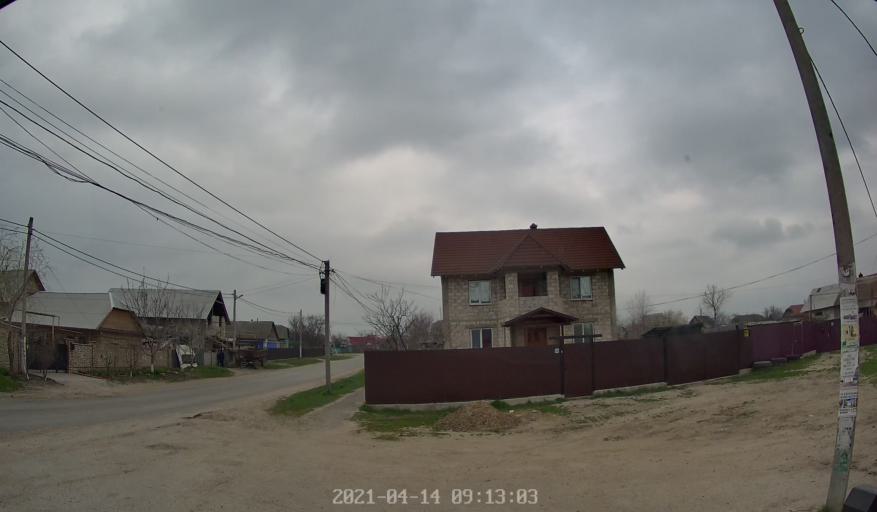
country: MD
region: Chisinau
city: Vadul lui Voda
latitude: 47.1011
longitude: 29.1120
